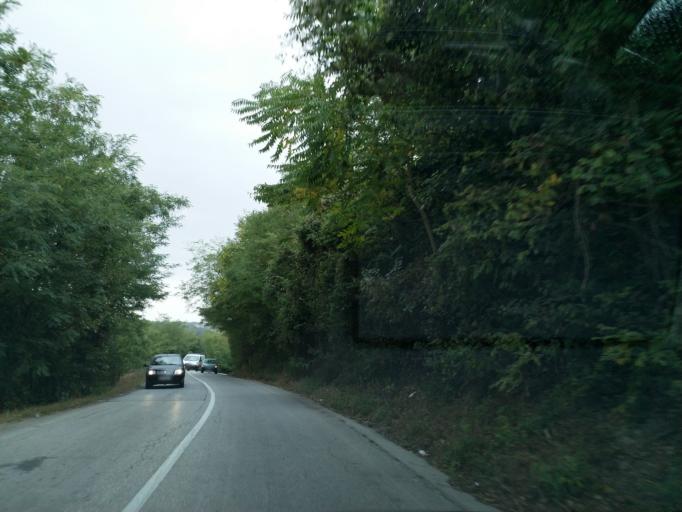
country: RS
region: Central Serbia
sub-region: Pomoravski Okrug
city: Jagodina
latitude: 44.0481
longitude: 21.1830
